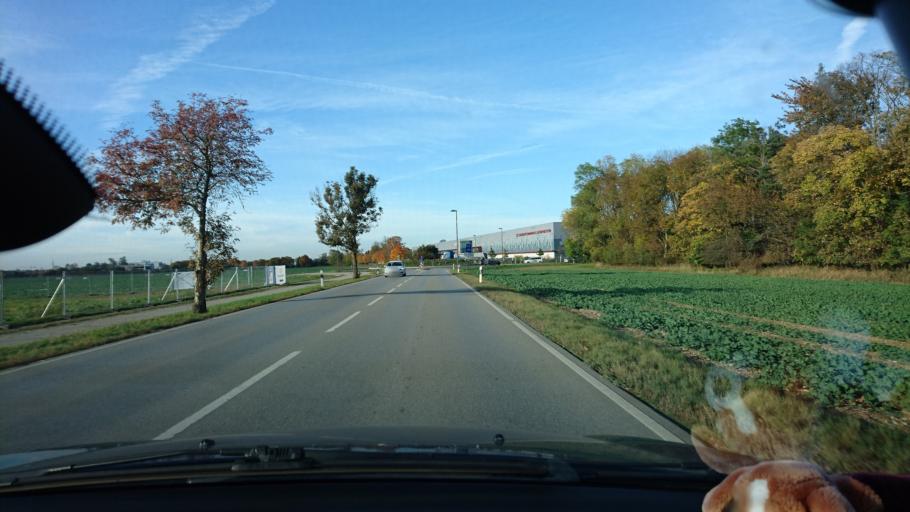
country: DE
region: Bavaria
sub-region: Upper Bavaria
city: Kirchheim bei Muenchen
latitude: 48.1592
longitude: 11.7845
